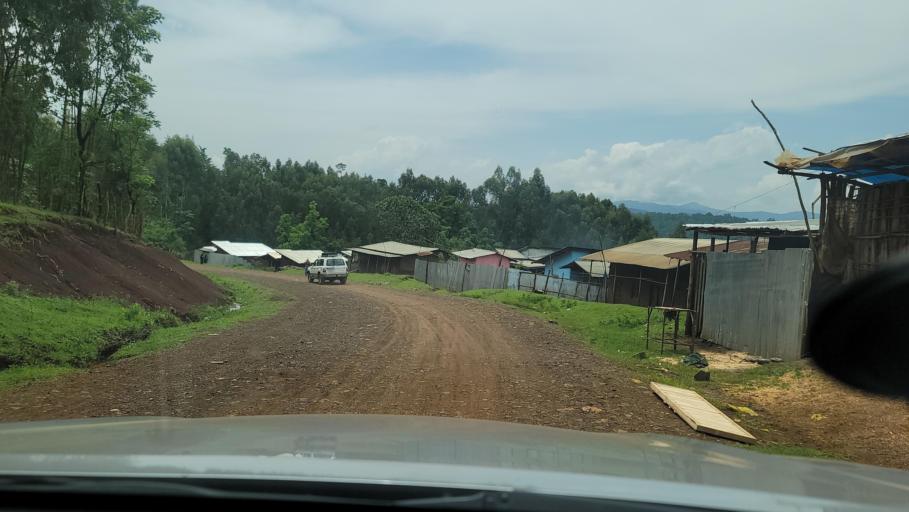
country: ET
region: Oromiya
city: Agaro
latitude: 7.7379
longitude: 36.2549
